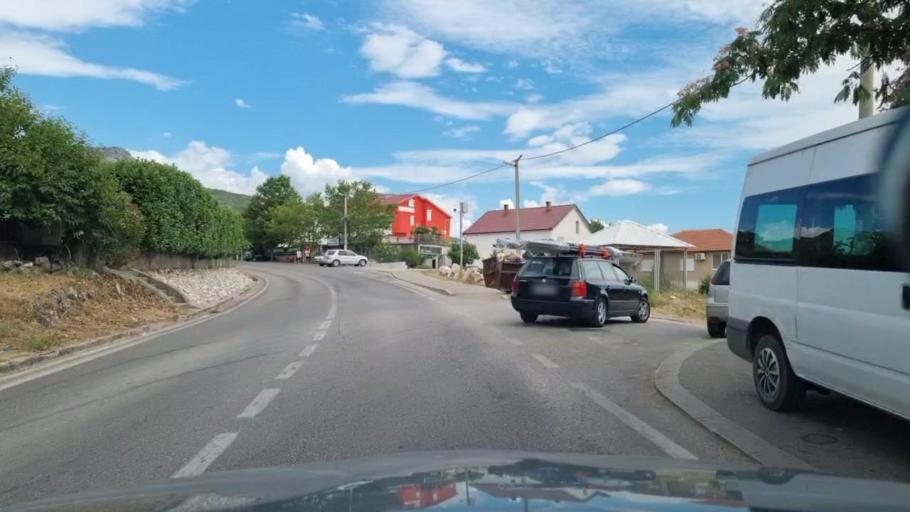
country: BA
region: Federation of Bosnia and Herzegovina
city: Blagaj
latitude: 43.2807
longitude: 17.8700
